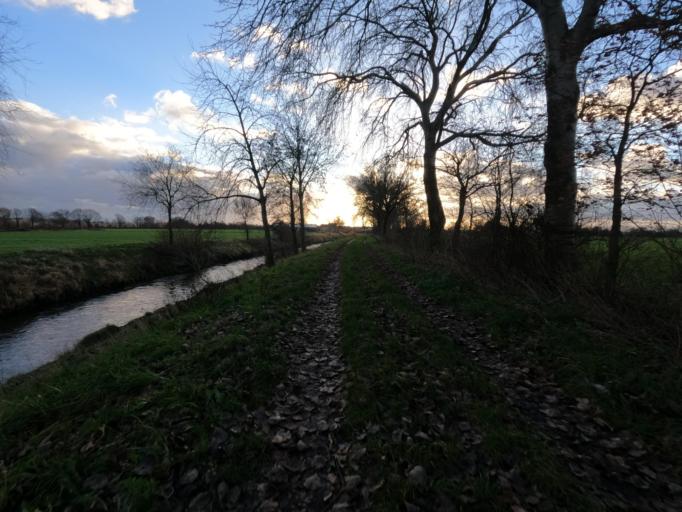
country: DE
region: North Rhine-Westphalia
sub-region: Regierungsbezirk Koln
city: Heinsberg
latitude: 51.0955
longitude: 6.1105
